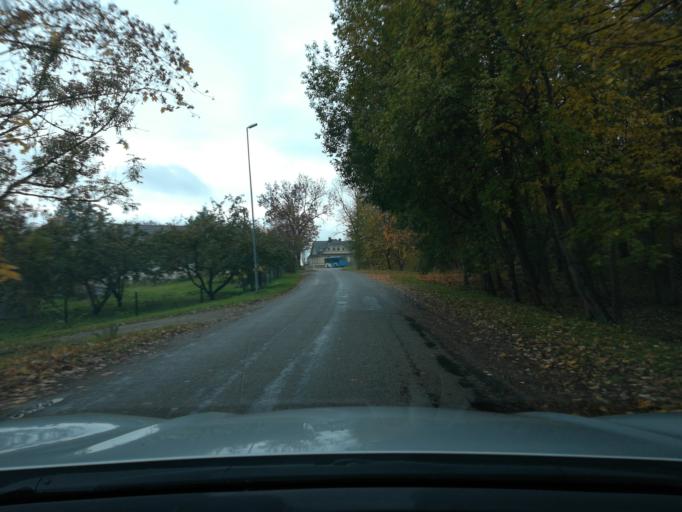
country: EE
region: Ida-Virumaa
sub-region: Johvi vald
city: Johvi
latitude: 59.1975
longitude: 27.5399
